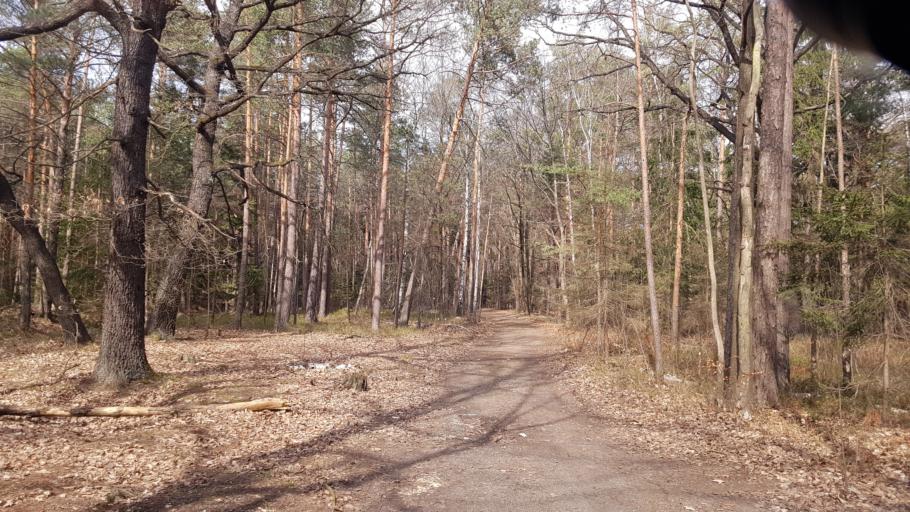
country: DE
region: Brandenburg
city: Lauchhammer
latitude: 51.5397
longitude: 13.6987
